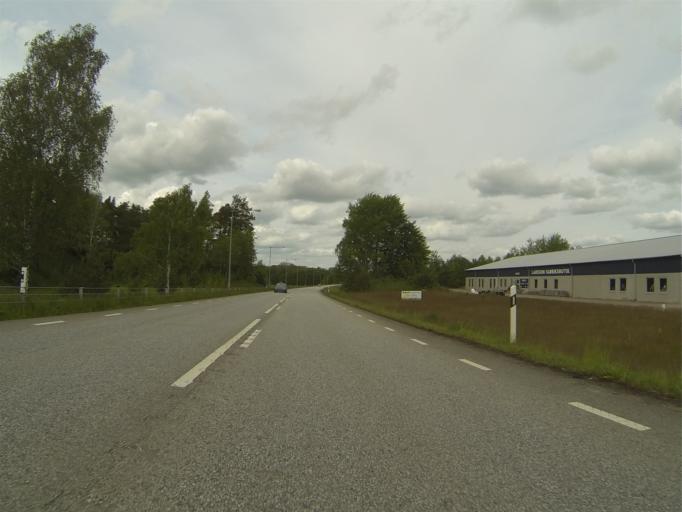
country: SE
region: Skane
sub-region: Sjobo Kommun
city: Sjoebo
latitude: 55.6374
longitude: 13.6825
